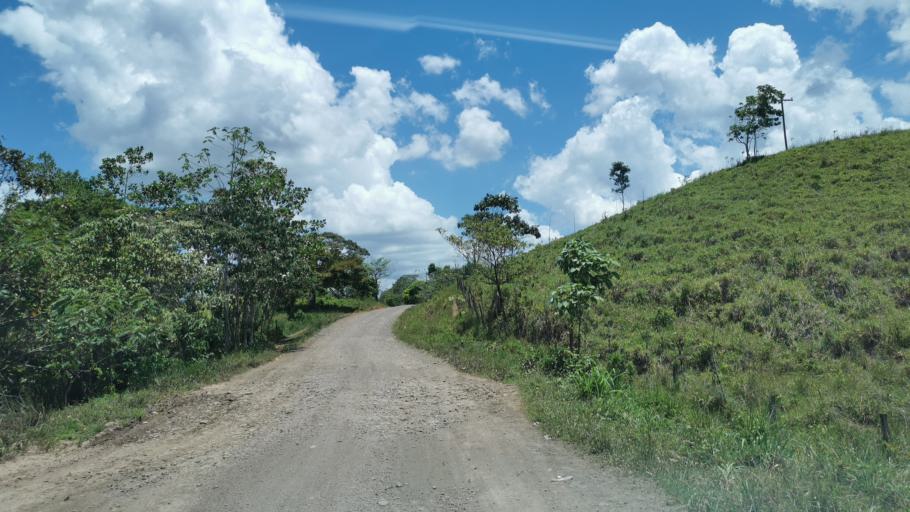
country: NI
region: Atlantico Sur
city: Rama
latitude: 12.3935
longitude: -84.3068
